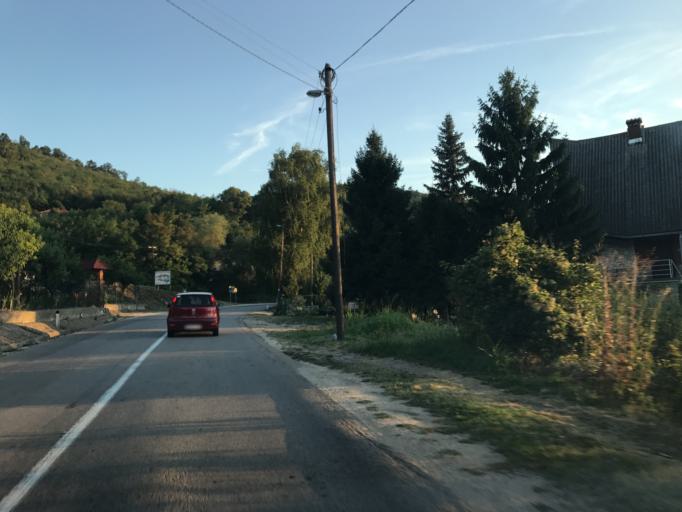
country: RS
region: Central Serbia
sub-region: Branicevski Okrug
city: Golubac
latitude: 44.6561
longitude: 21.6554
